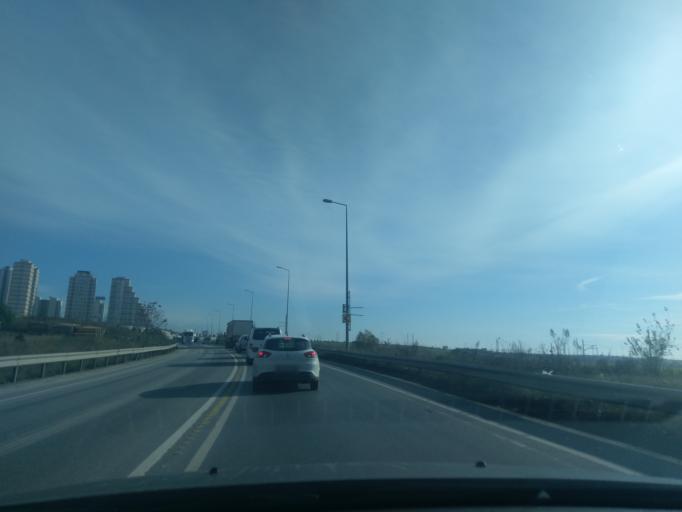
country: TR
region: Istanbul
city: Esenyurt
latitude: 41.0563
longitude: 28.7062
